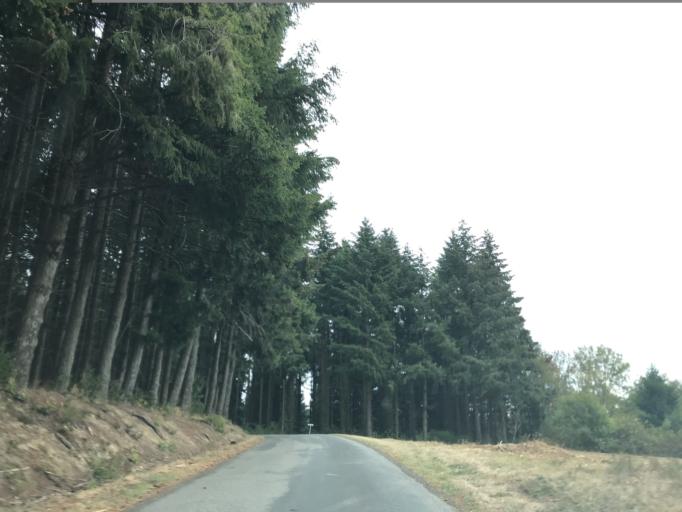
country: FR
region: Auvergne
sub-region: Departement du Puy-de-Dome
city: Thiers
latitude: 45.8366
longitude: 3.5669
